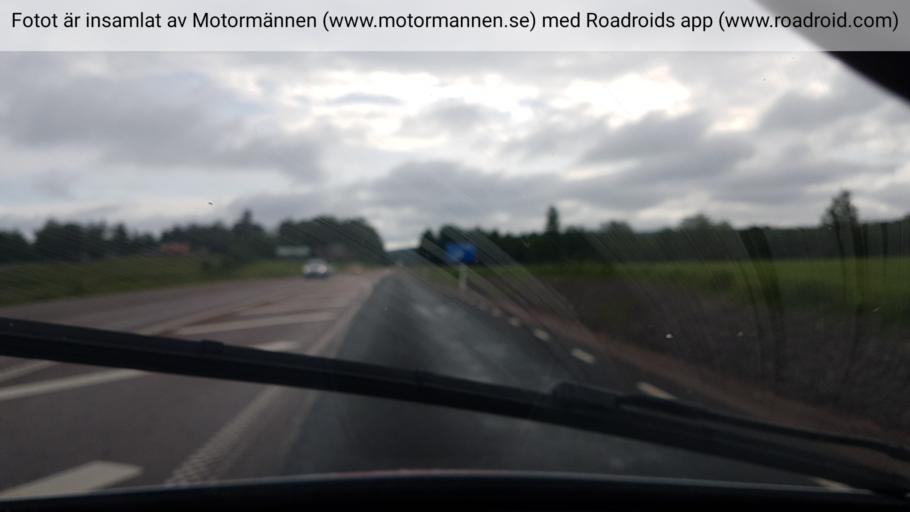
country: SE
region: Vaestra Goetaland
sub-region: Tibro Kommun
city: Tibro
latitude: 58.4553
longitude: 14.2225
